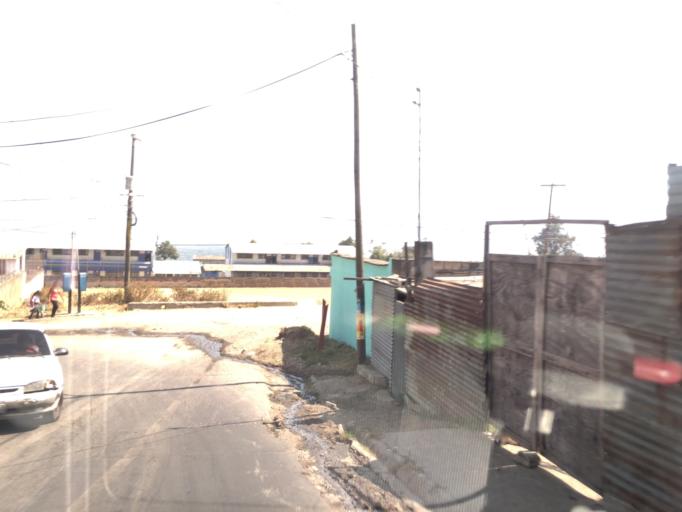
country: GT
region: Guatemala
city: Amatitlan
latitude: 14.5007
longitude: -90.5929
